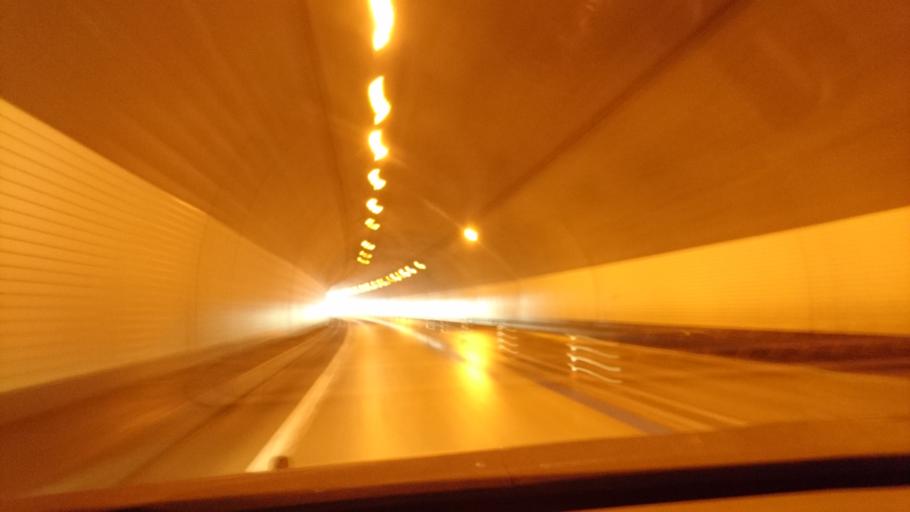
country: JP
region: Iwate
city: Miyako
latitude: 39.8725
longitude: 141.9392
